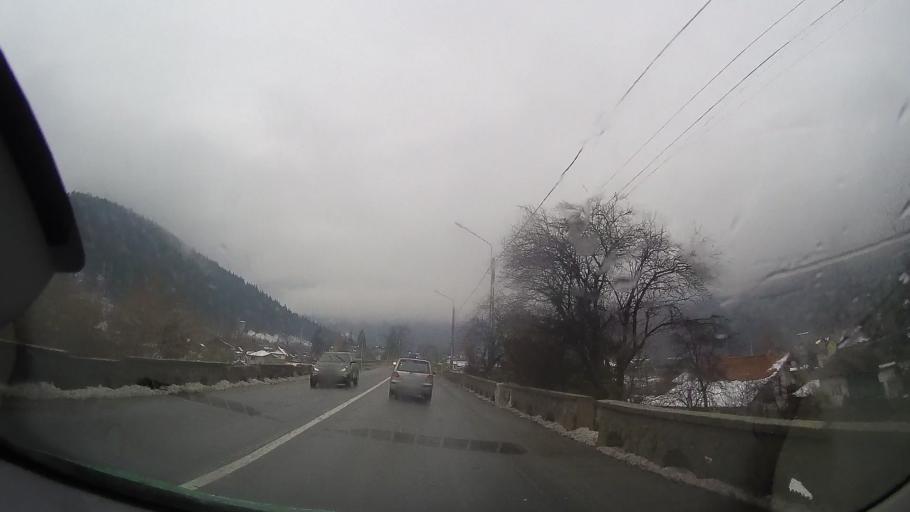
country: RO
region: Neamt
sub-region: Comuna Bicaz
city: Dodeni
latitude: 46.9068
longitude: 26.1061
